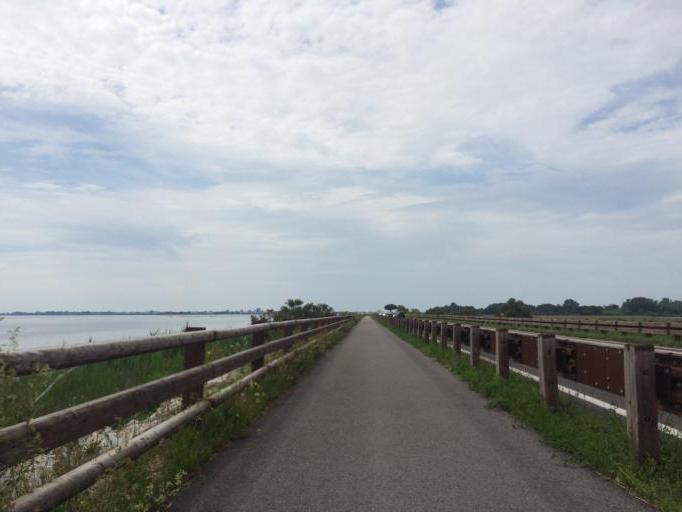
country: IT
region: Friuli Venezia Giulia
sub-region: Provincia di Gorizia
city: Grado
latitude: 45.7205
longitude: 13.3859
